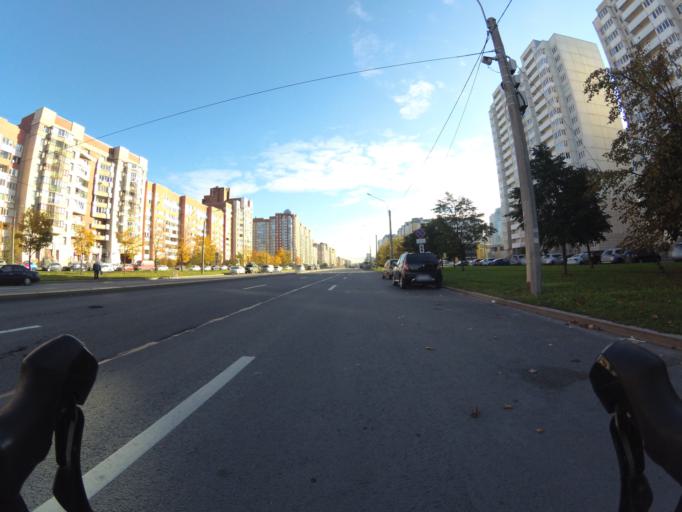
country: RU
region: Leningrad
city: Untolovo
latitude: 60.0075
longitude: 30.2073
